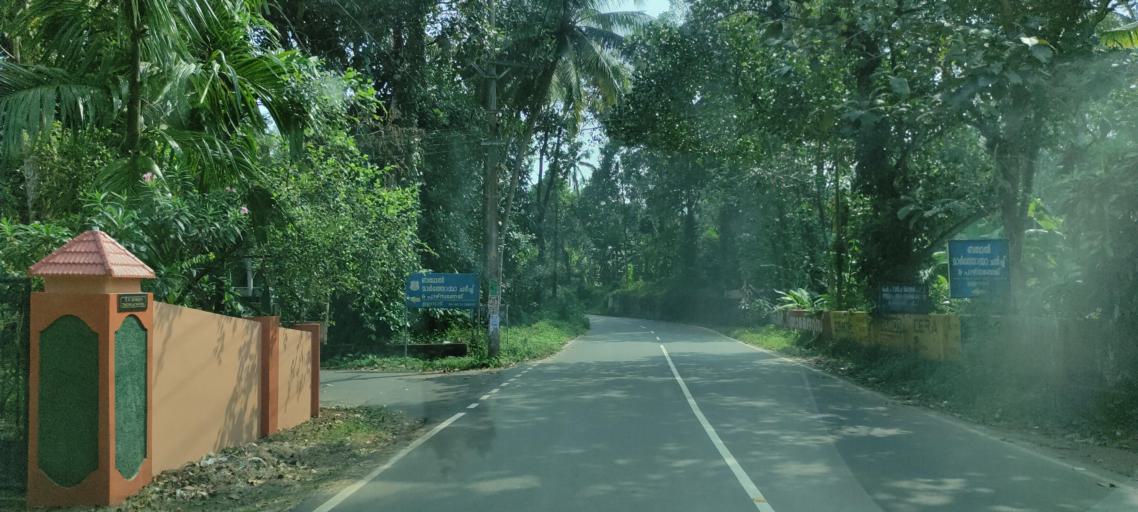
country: IN
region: Kerala
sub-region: Pattanamtitta
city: Adur
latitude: 9.2352
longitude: 76.6974
